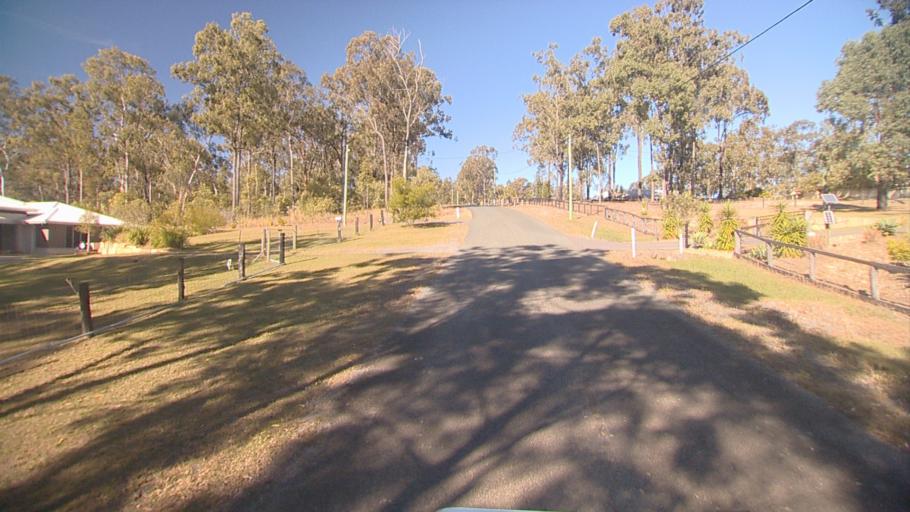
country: AU
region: Queensland
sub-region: Ipswich
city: Springfield Lakes
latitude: -27.7002
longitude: 152.9263
